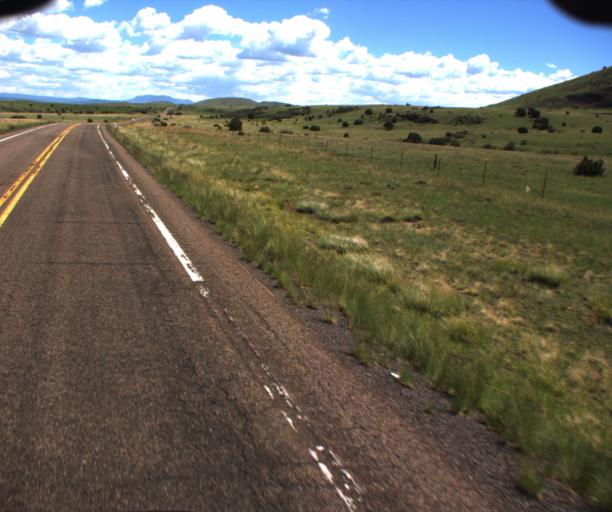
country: US
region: Arizona
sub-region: Apache County
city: Springerville
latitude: 34.2357
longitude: -109.5013
